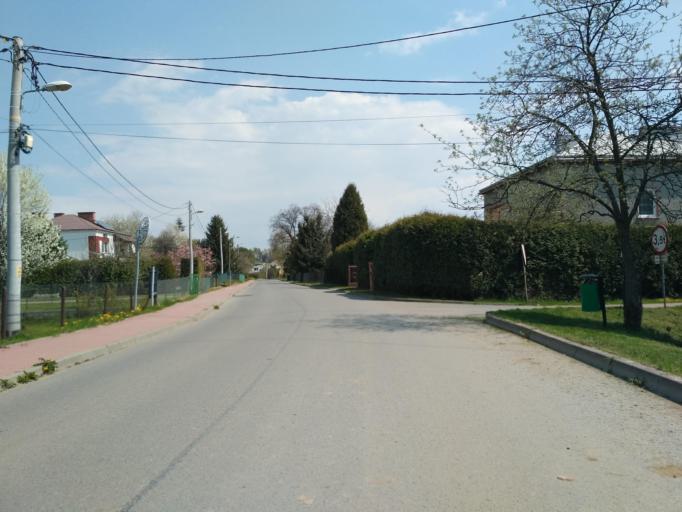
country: PL
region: Subcarpathian Voivodeship
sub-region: Powiat krosnienski
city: Jedlicze
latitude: 49.7267
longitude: 21.6269
